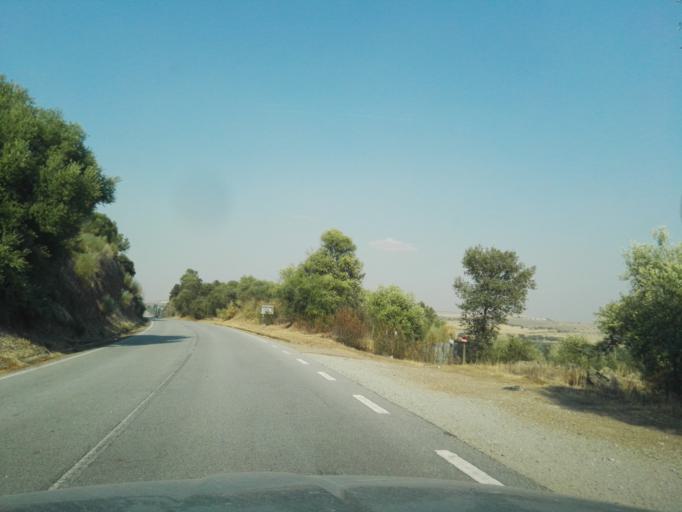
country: PT
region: Portalegre
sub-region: Campo Maior
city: Campo Maior
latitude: 38.9956
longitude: -7.1495
